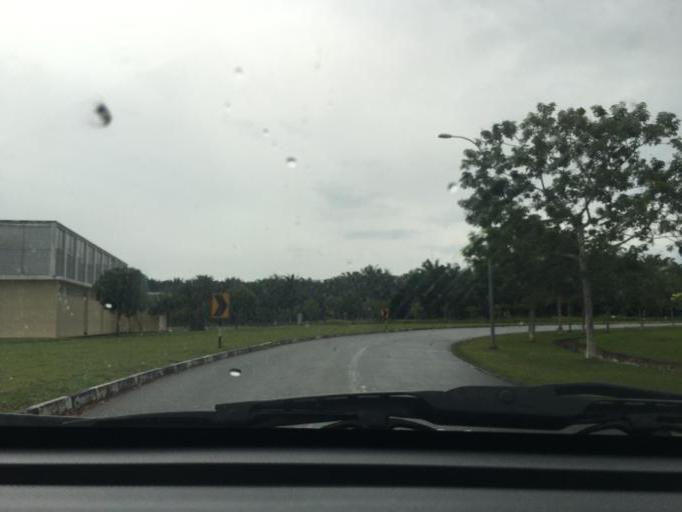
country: MY
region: Kedah
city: Sungai Petani
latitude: 5.5864
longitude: 100.6424
